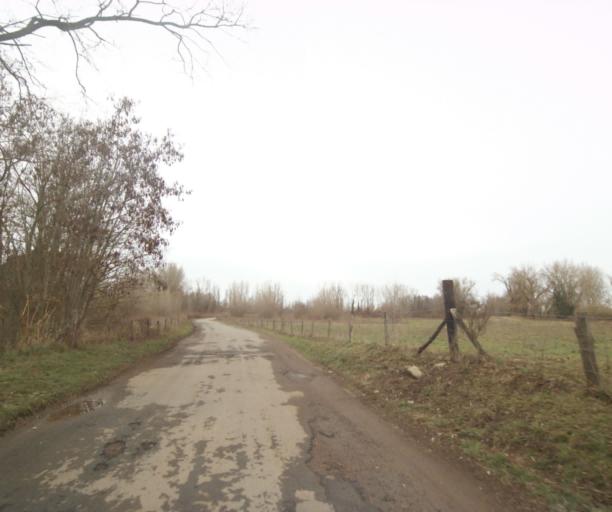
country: FR
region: Rhone-Alpes
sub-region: Departement de la Loire
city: Perreux
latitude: 46.0585
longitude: 4.1081
